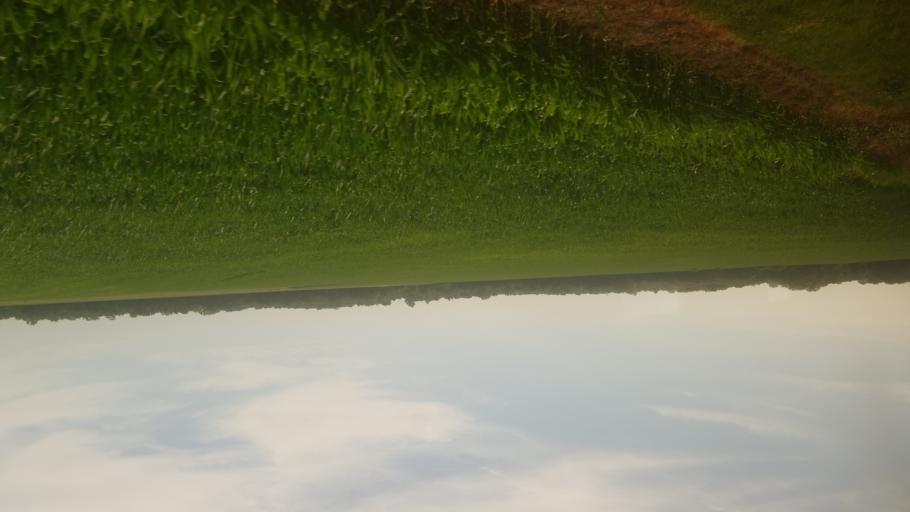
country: US
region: Kansas
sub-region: Douglas County
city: Eudora
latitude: 38.9495
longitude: -95.1198
